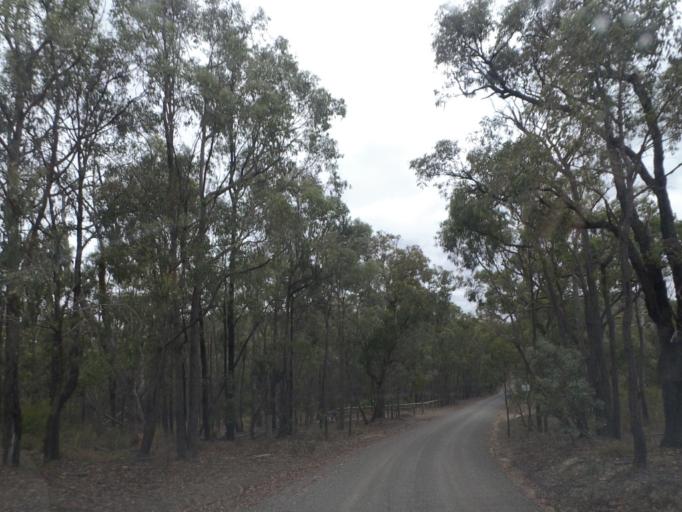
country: AU
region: Victoria
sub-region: Yarra Ranges
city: Chirnside Park
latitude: -37.6896
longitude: 145.3113
